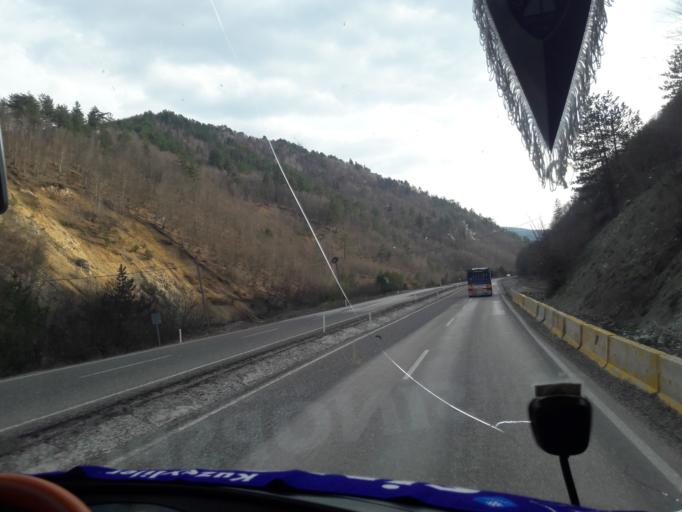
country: TR
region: Kastamonu
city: Kuzyaka
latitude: 41.1351
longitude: 33.7760
